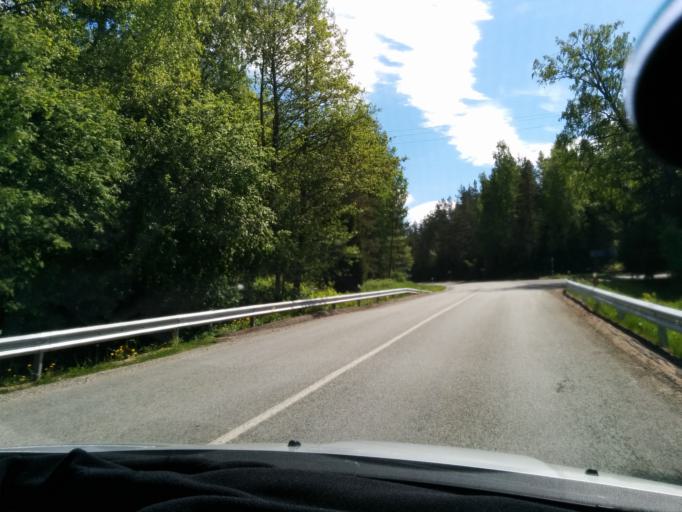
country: EE
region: Laeaene-Virumaa
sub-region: Kadrina vald
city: Kadrina
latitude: 59.5578
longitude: 25.9937
